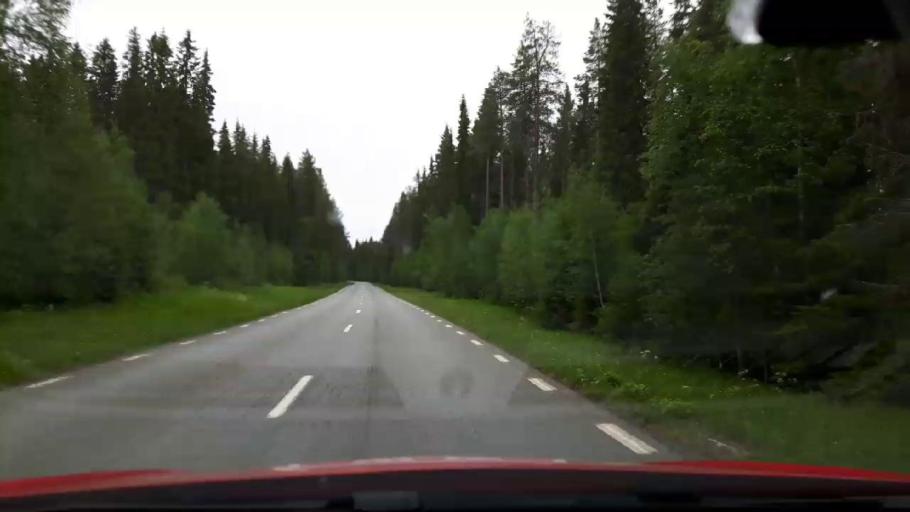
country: SE
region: Jaemtland
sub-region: Stroemsunds Kommun
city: Stroemsund
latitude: 63.4588
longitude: 15.4585
